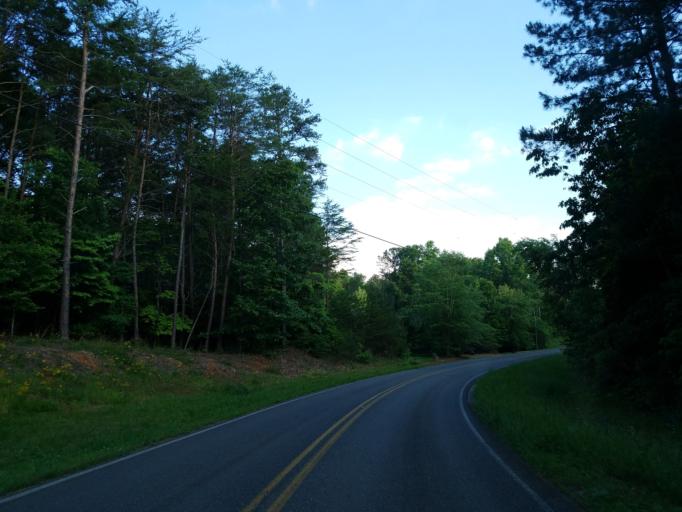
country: US
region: Georgia
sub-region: Cherokee County
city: Ball Ground
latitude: 34.3190
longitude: -84.3694
